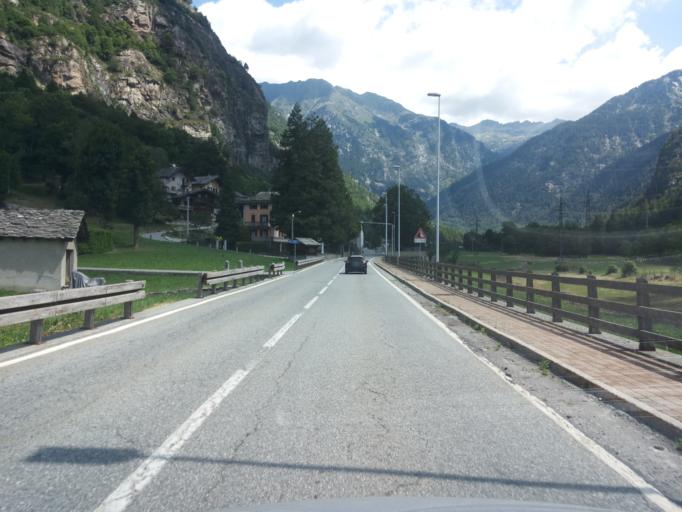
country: IT
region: Aosta Valley
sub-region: Valle d'Aosta
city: Issime
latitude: 45.6930
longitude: 7.8586
